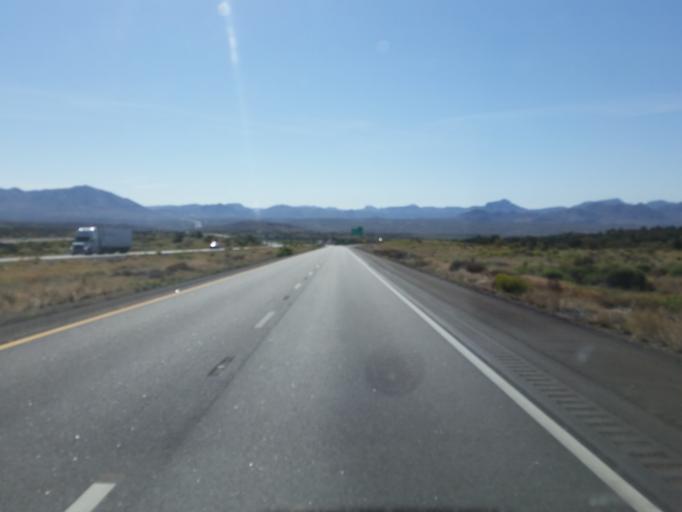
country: US
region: Arizona
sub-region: Mohave County
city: New Kingman-Butler
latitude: 35.1600
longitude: -113.7041
